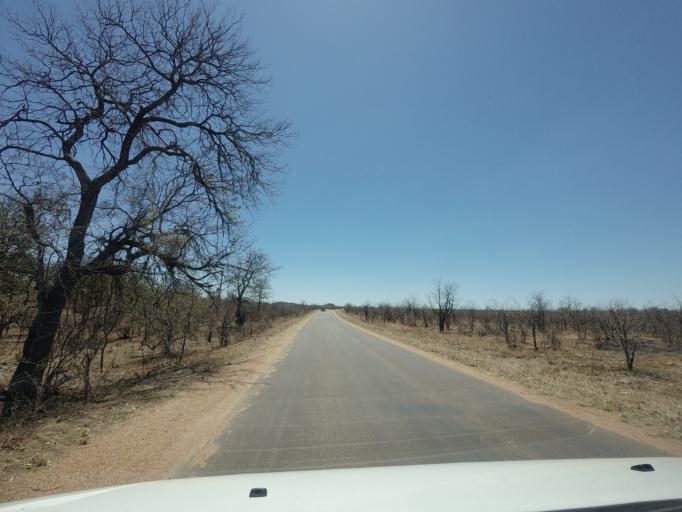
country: ZA
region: Limpopo
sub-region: Mopani District Municipality
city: Phalaborwa
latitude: -23.5389
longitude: 31.4232
